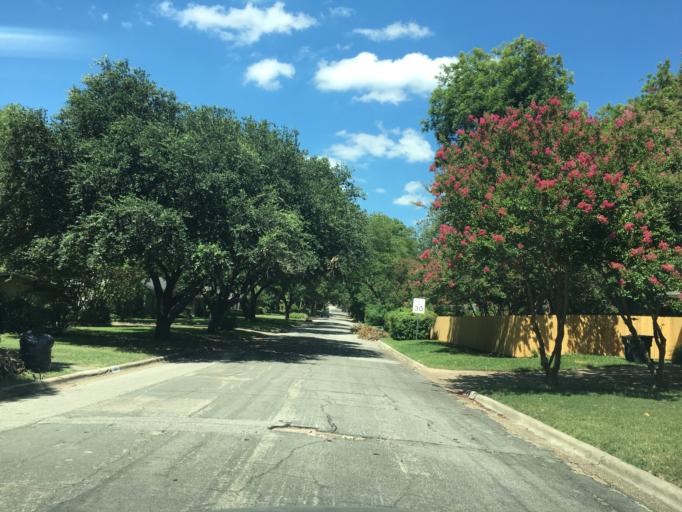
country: US
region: Texas
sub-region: Dallas County
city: Highland Park
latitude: 32.8434
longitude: -96.7017
